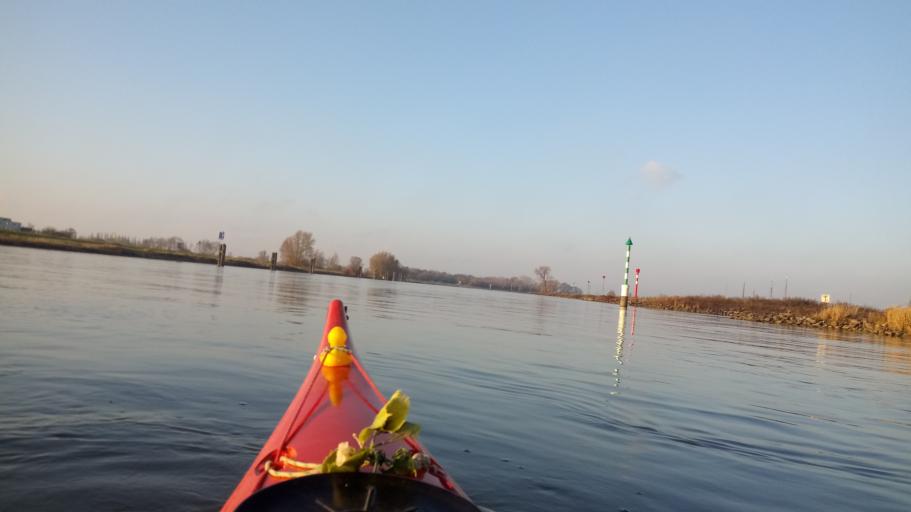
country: NL
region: Gelderland
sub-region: Gemeente Zutphen
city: Zutphen
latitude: 52.1449
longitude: 6.1882
